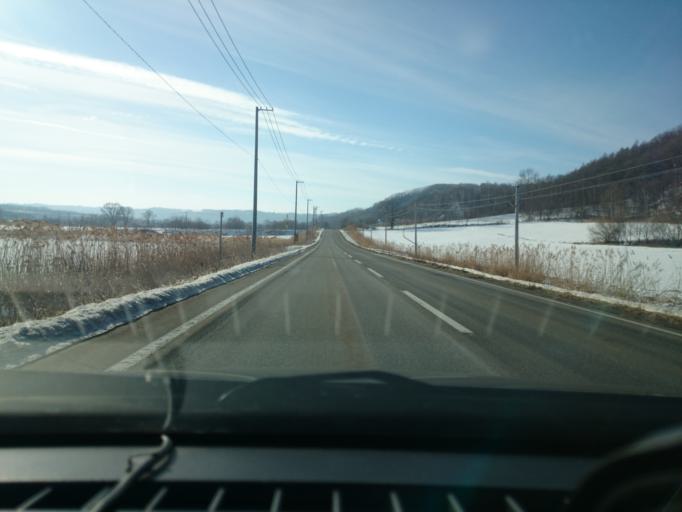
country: JP
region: Hokkaido
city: Otofuke
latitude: 43.2608
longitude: 143.5753
